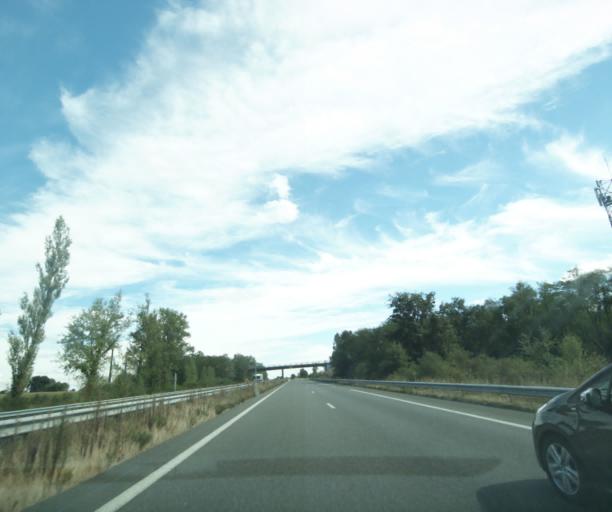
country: FR
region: Midi-Pyrenees
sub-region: Departement du Tarn-et-Garonne
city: Auvillar
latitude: 44.0561
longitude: 0.9520
